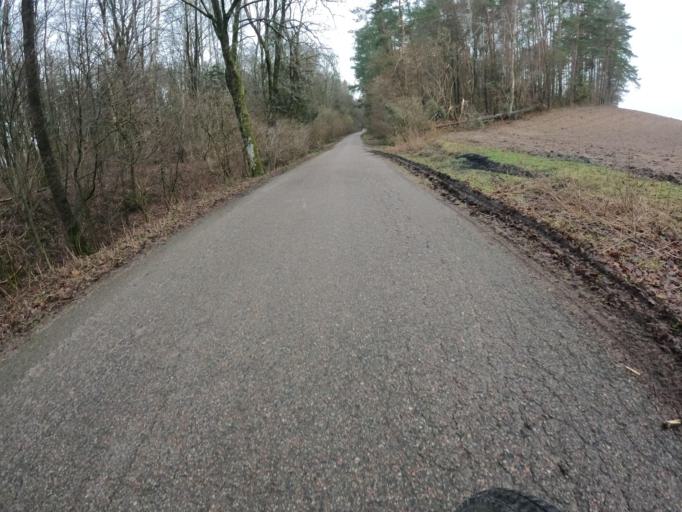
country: PL
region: West Pomeranian Voivodeship
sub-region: Powiat slawienski
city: Slawno
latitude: 54.2609
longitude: 16.6654
